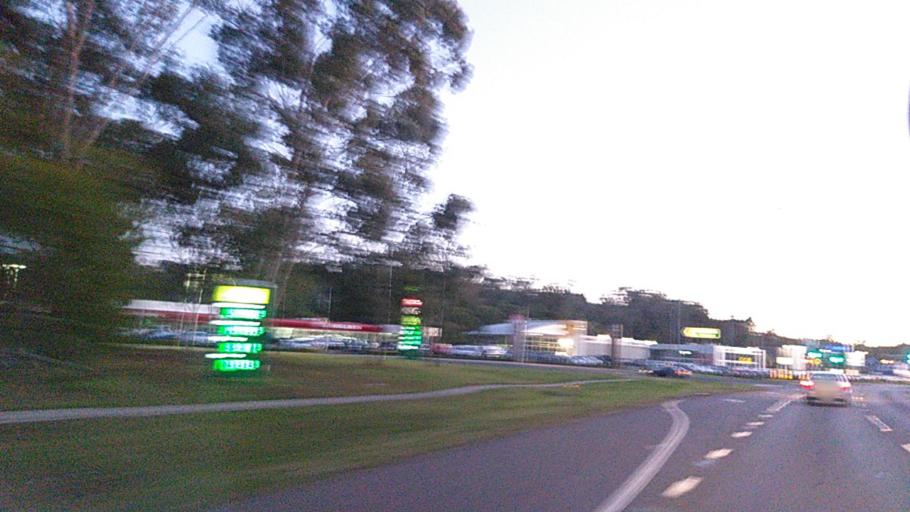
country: AU
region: New South Wales
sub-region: Campbelltown Municipality
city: Leumeah
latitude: -34.0533
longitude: 150.8239
